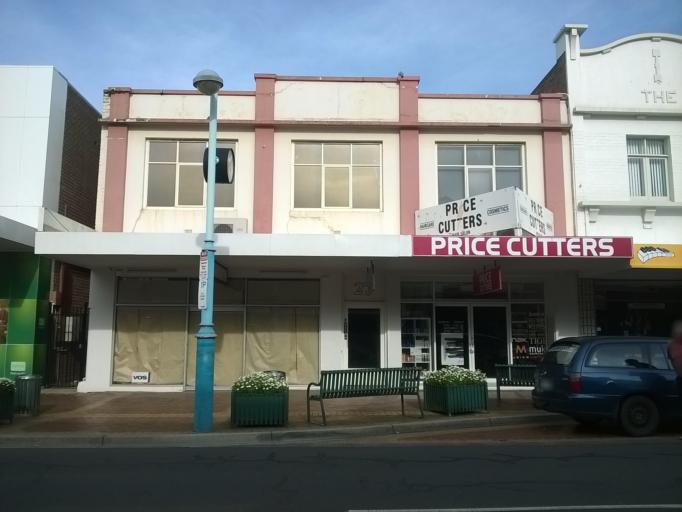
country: AU
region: Tasmania
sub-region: Burnie
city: Burnie
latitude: -41.0524
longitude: 145.9057
